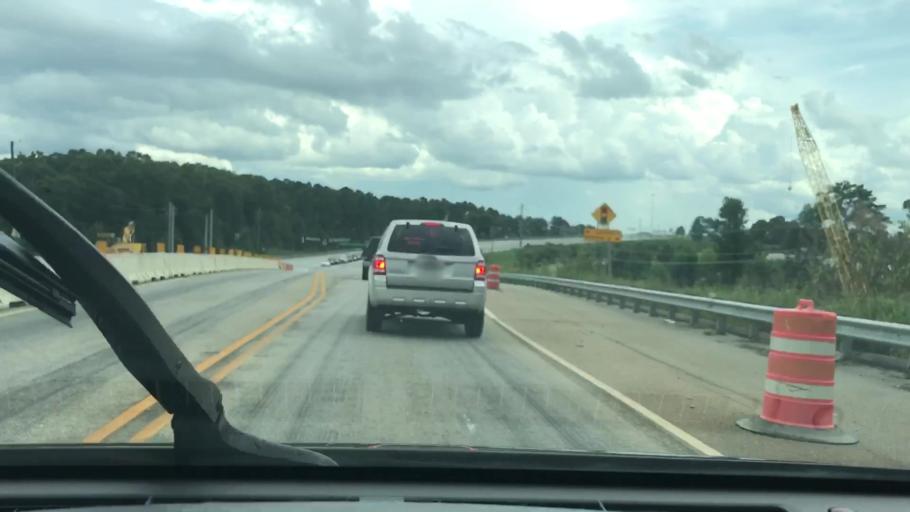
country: US
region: Georgia
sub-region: Newton County
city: Covington
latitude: 33.6188
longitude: -83.8243
